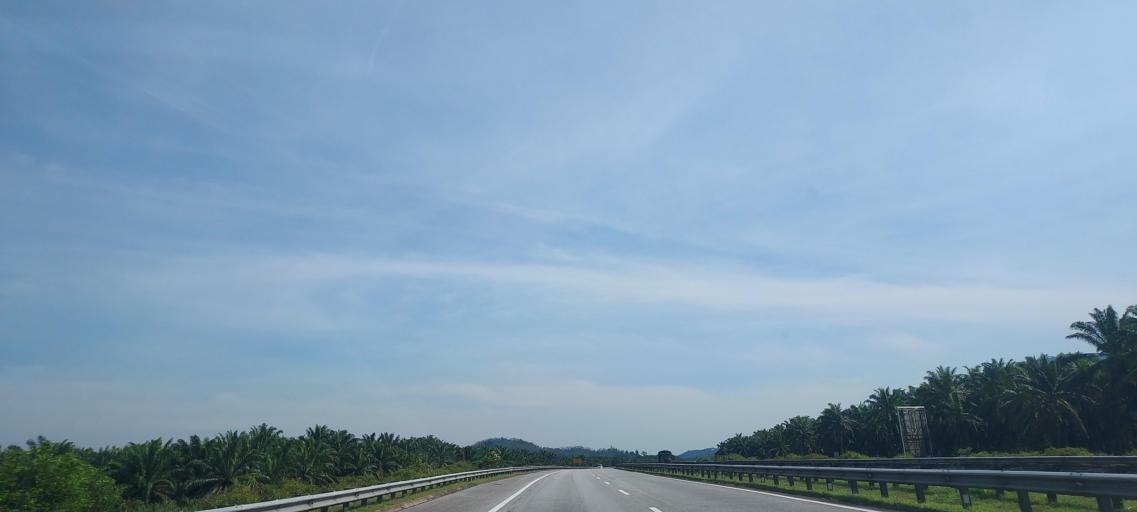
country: MY
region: Terengganu
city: Marang
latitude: 4.9624
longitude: 103.0819
